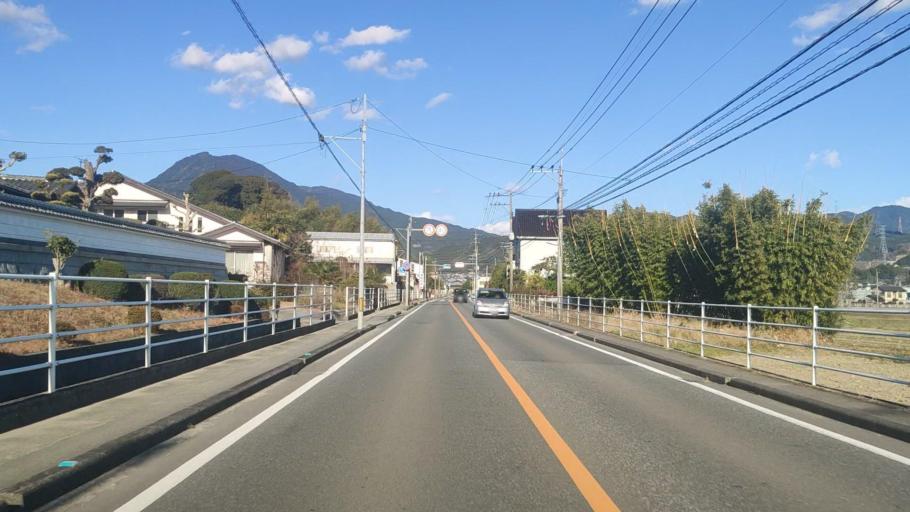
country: JP
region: Fukuoka
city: Dazaifu
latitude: 33.4969
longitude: 130.5469
